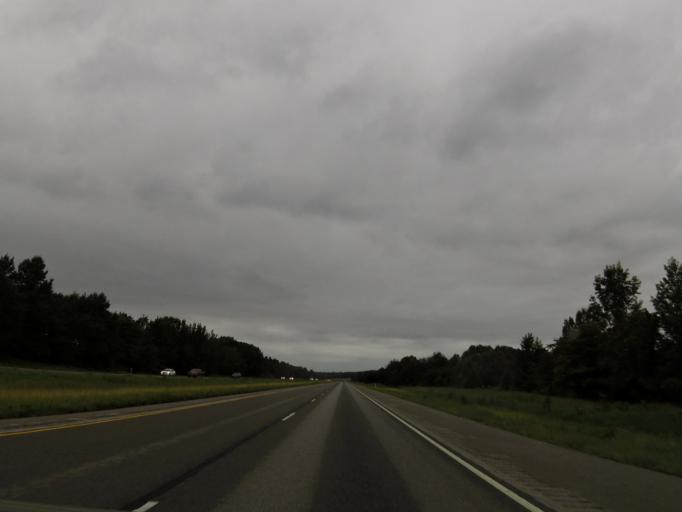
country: US
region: Illinois
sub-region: Johnson County
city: Vienna
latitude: 37.3294
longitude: -88.7719
